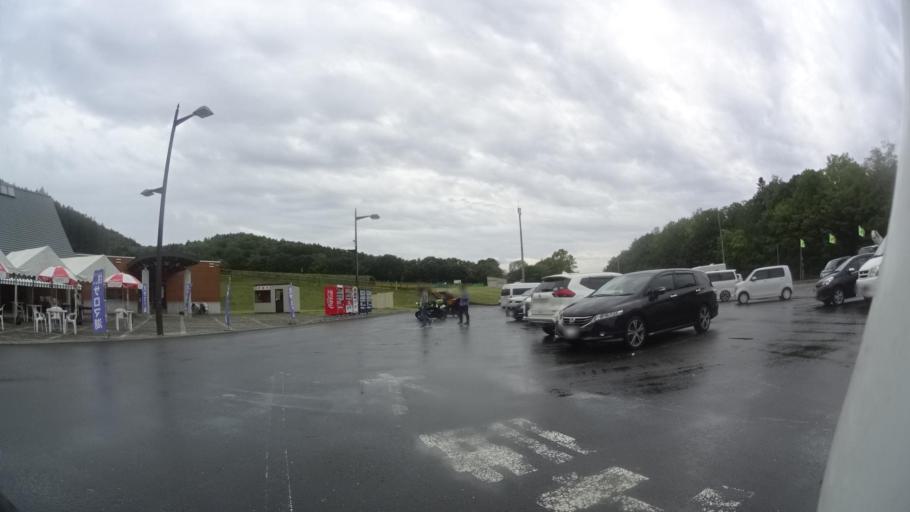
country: JP
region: Hokkaido
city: Kitami
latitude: 44.1000
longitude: 143.8234
